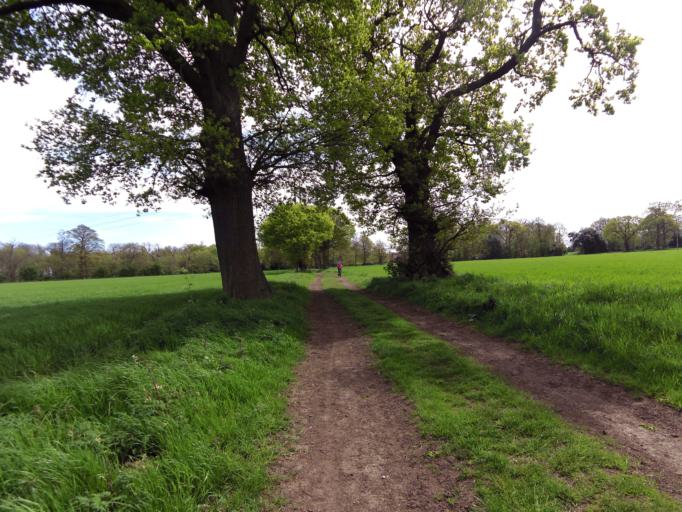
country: GB
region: England
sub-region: Suffolk
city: Ipswich
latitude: 51.9971
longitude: 1.1446
